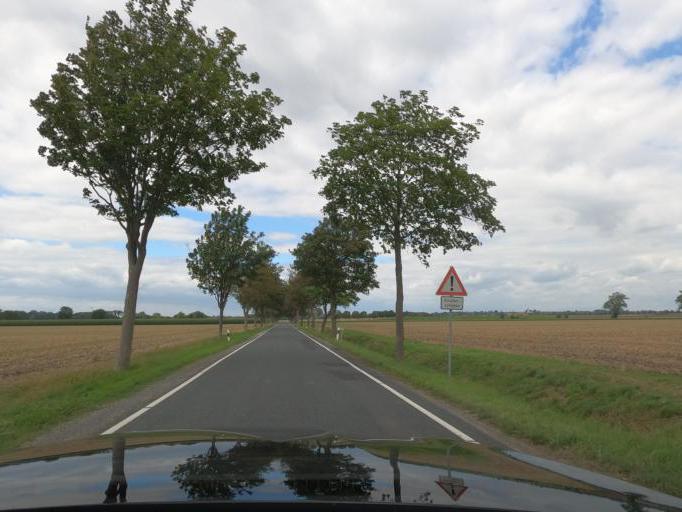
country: DE
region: Lower Saxony
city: Hohenhameln
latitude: 52.2249
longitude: 10.0666
